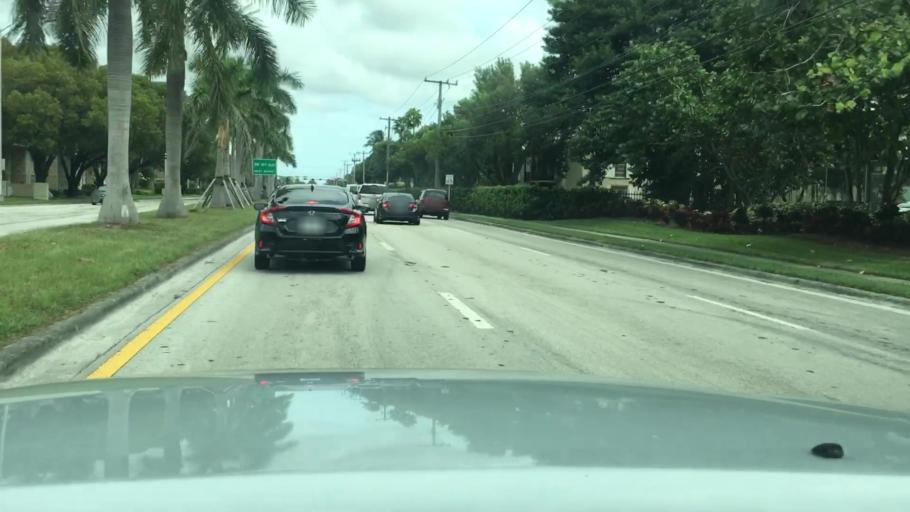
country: US
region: Florida
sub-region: Miami-Dade County
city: Sunset
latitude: 25.6868
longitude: -80.3696
